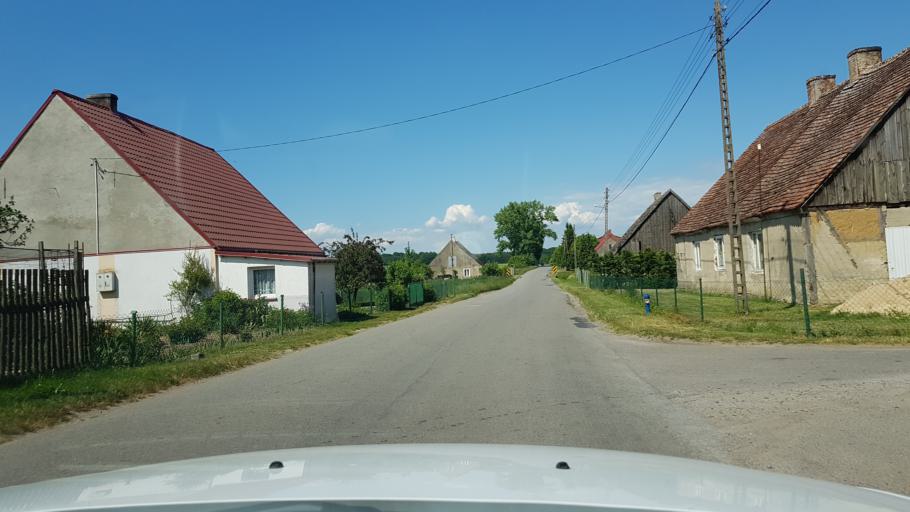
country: PL
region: West Pomeranian Voivodeship
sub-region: Powiat gryfinski
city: Banie
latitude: 53.0430
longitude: 14.6246
